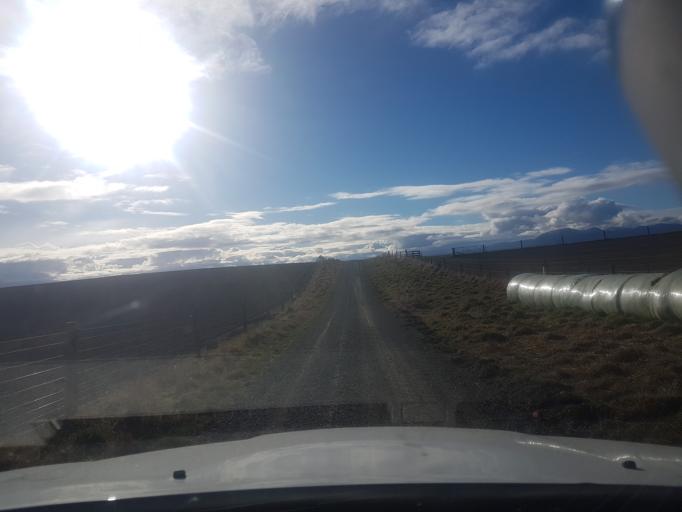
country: NZ
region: Canterbury
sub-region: Timaru District
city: Pleasant Point
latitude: -44.1763
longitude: 170.8900
